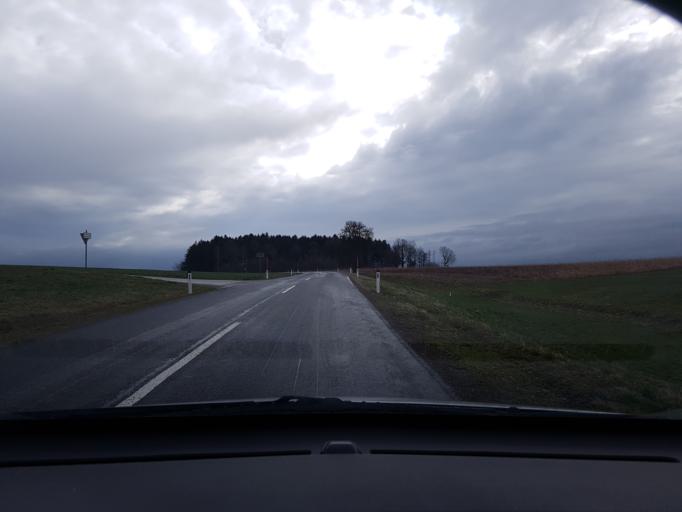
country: AT
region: Upper Austria
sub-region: Politischer Bezirk Linz-Land
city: Sankt Florian
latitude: 48.1527
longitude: 14.3601
